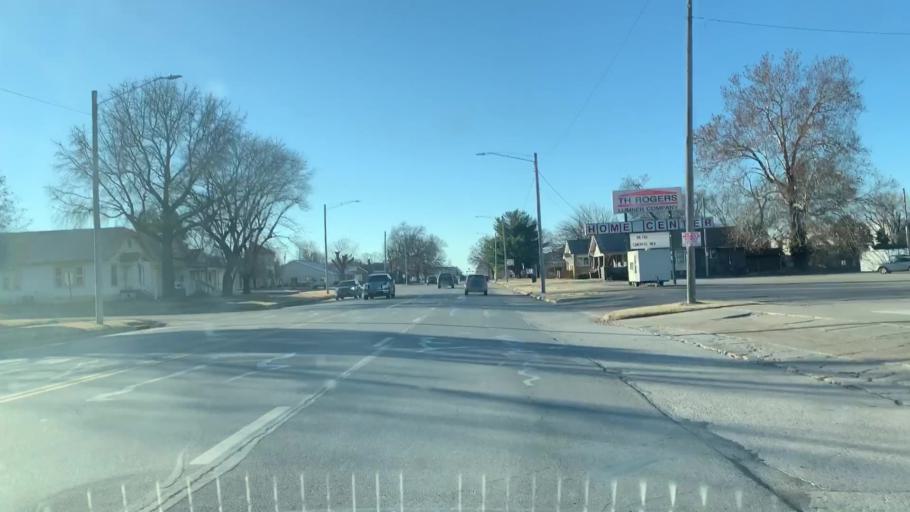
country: US
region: Kansas
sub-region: Crawford County
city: Pittsburg
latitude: 37.4235
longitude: -94.7050
